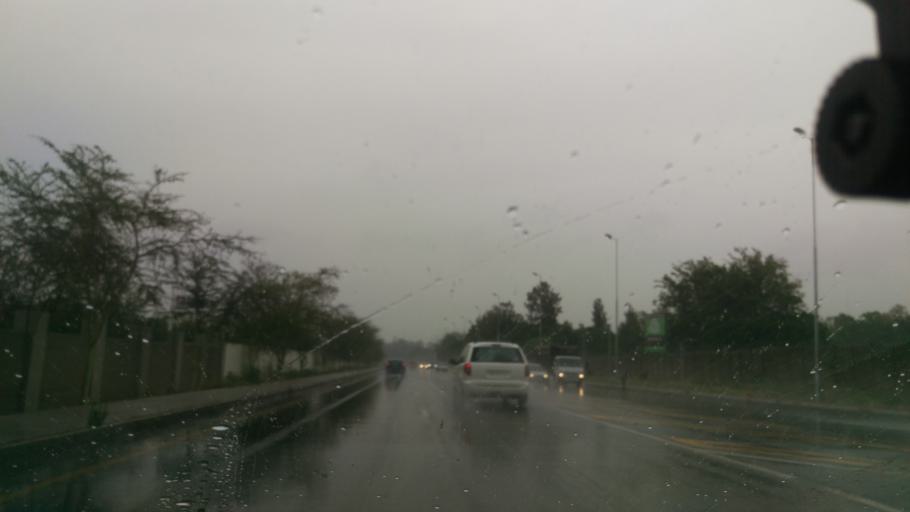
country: ZA
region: Gauteng
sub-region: City of Johannesburg Metropolitan Municipality
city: Diepsloot
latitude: -25.9893
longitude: 27.9843
